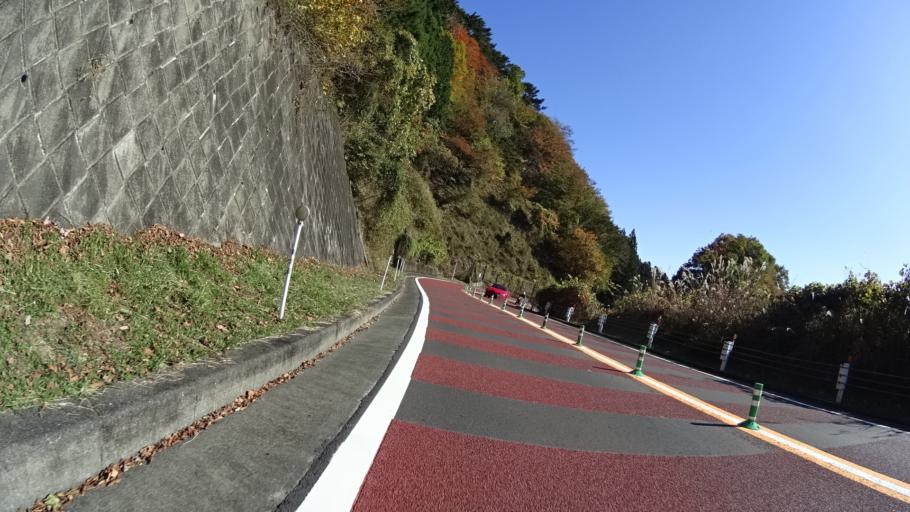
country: JP
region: Yamanashi
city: Uenohara
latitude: 35.7311
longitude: 139.0427
